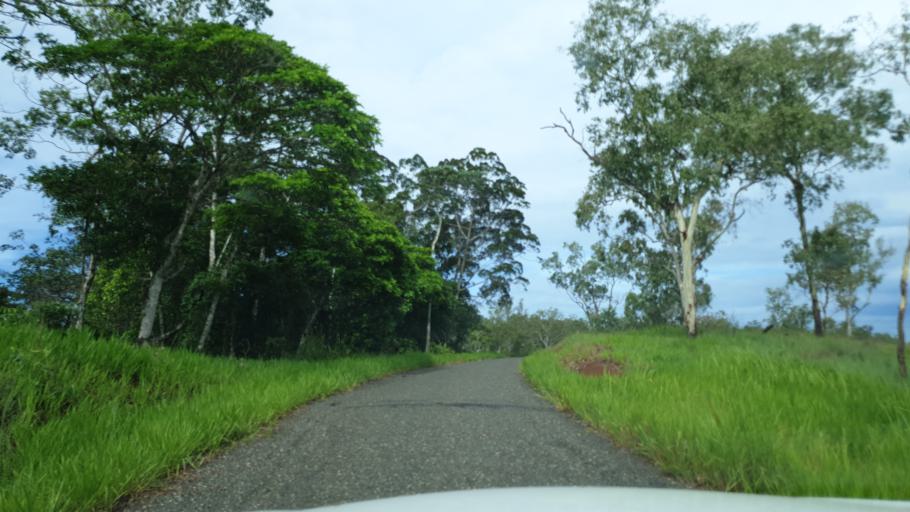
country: PG
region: National Capital
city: Port Moresby
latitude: -9.4353
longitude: 147.3837
